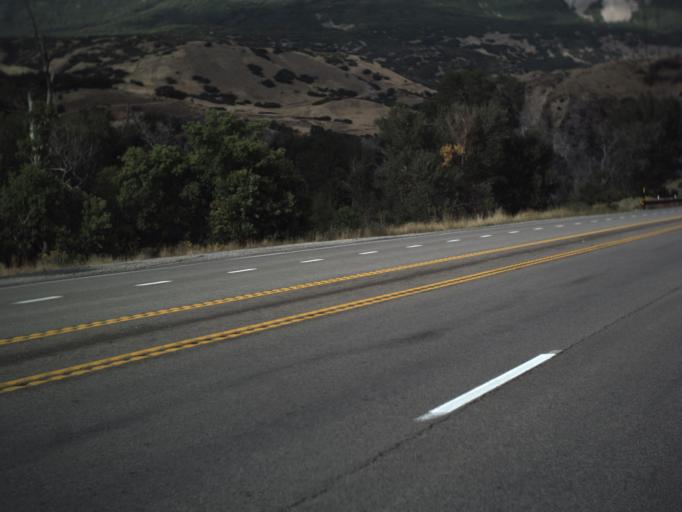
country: US
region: Utah
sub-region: Utah County
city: Orem
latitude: 40.3167
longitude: -111.6511
